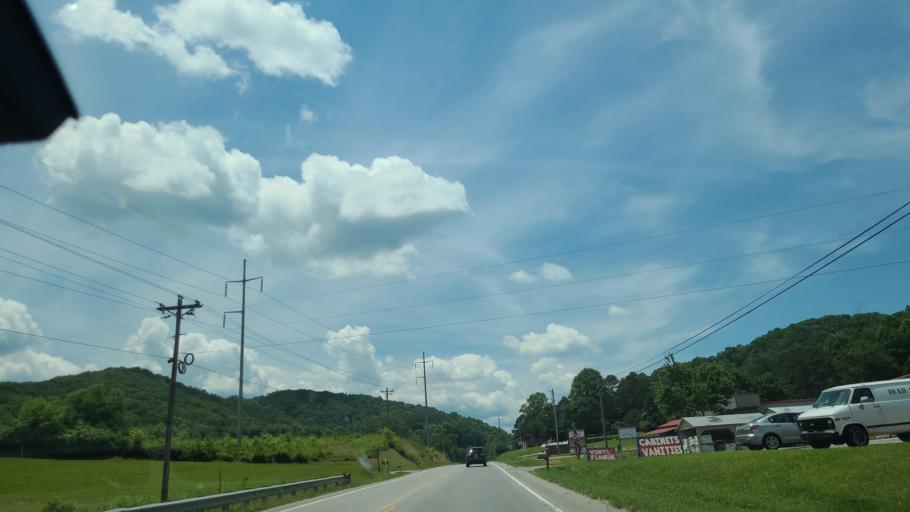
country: US
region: North Carolina
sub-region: Clay County
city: Hayesville
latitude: 35.0332
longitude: -83.8519
